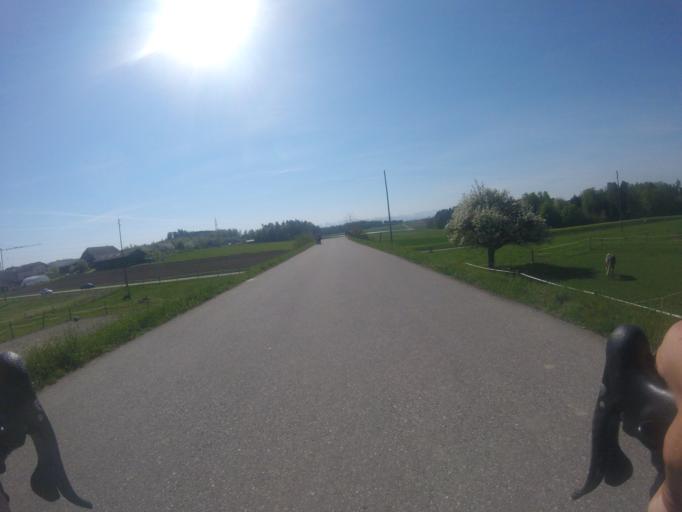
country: CH
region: Bern
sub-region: Bern-Mittelland District
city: Ferenbalm
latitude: 46.9420
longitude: 7.2233
